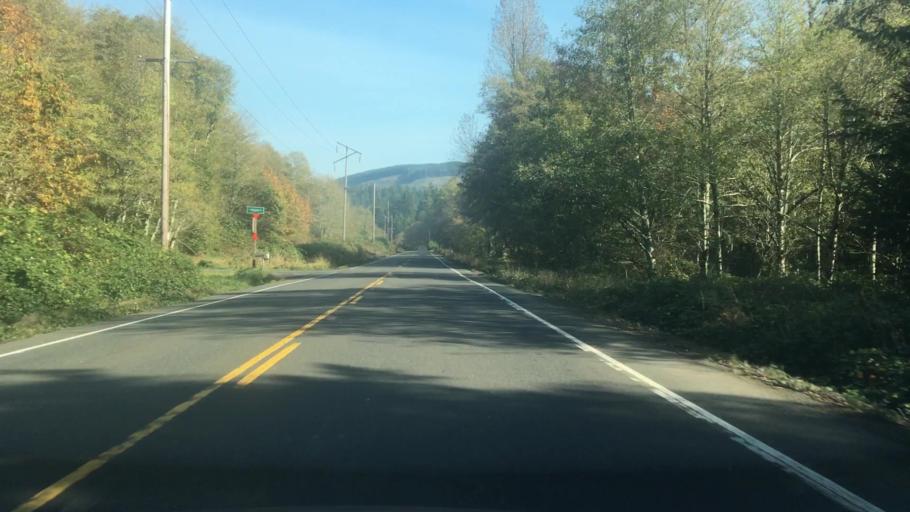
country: US
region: Oregon
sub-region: Lincoln County
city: Rose Lodge
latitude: 45.0222
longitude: -123.8385
